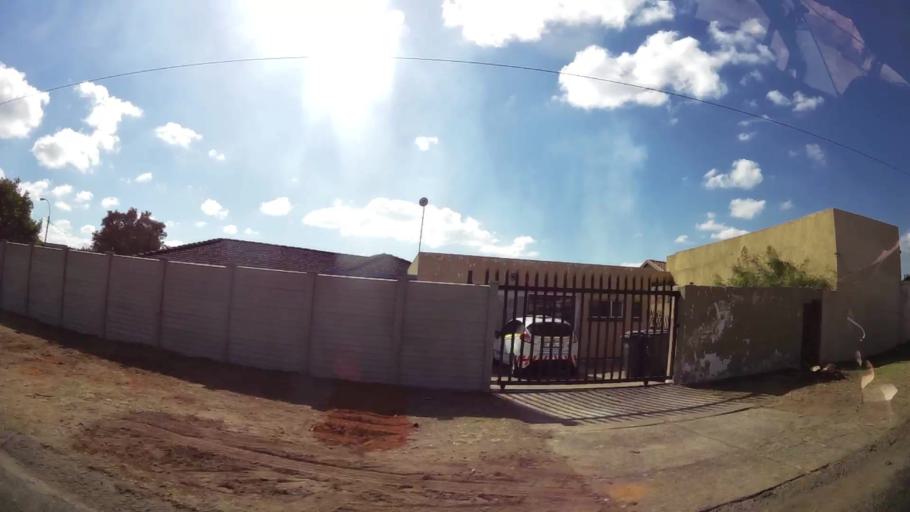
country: ZA
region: Gauteng
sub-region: City of Johannesburg Metropolitan Municipality
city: Roodepoort
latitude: -26.1182
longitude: 27.8389
